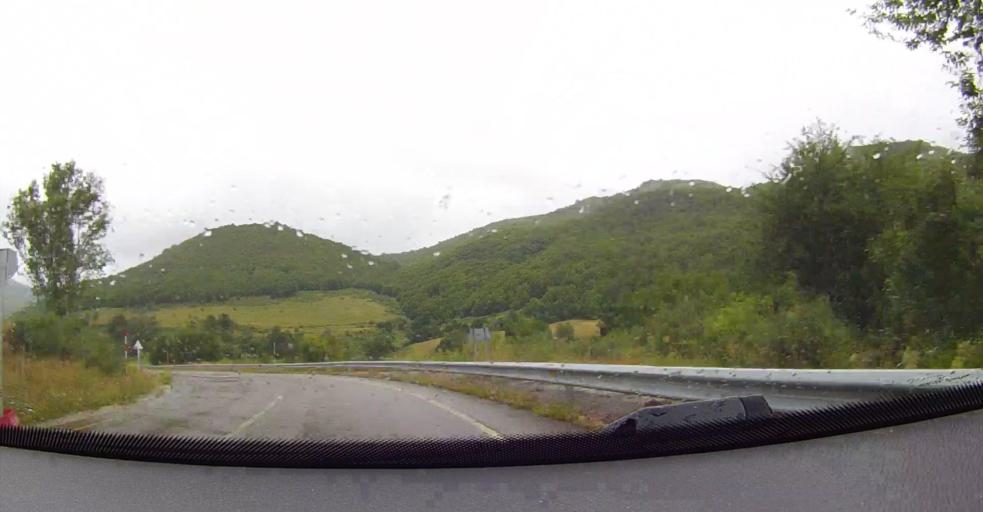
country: ES
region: Castille and Leon
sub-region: Provincia de Leon
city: Marana
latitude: 43.0711
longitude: -5.1645
